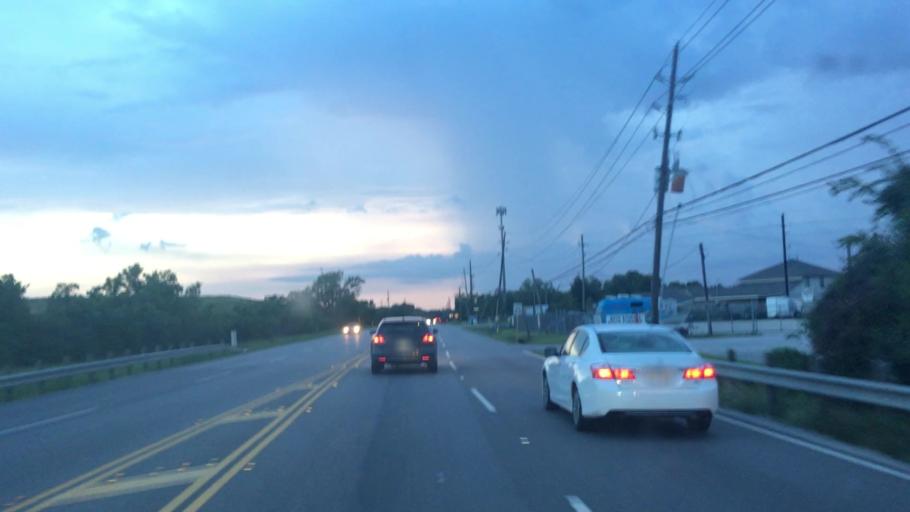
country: US
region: Texas
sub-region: Harris County
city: Humble
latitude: 29.9692
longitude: -95.2349
